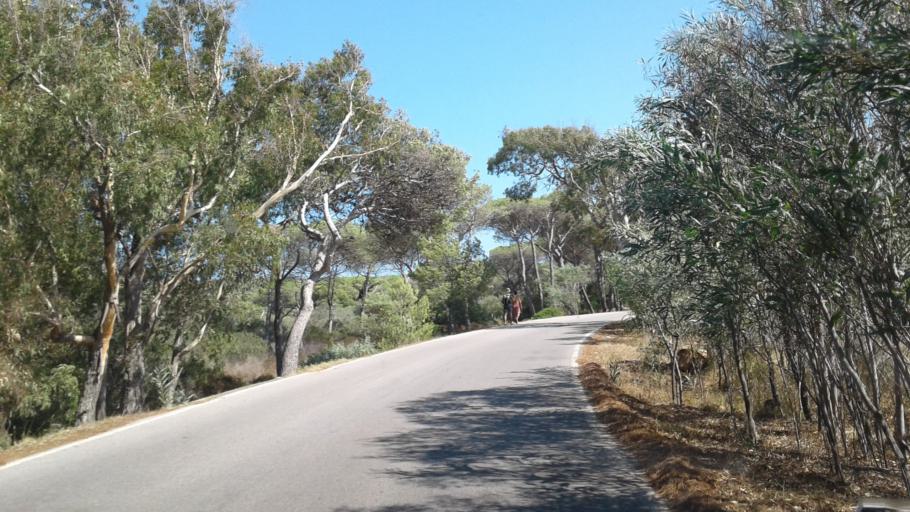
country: IT
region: Sardinia
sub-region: Provincia di Olbia-Tempio
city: La Maddalena
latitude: 41.2140
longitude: 9.4540
